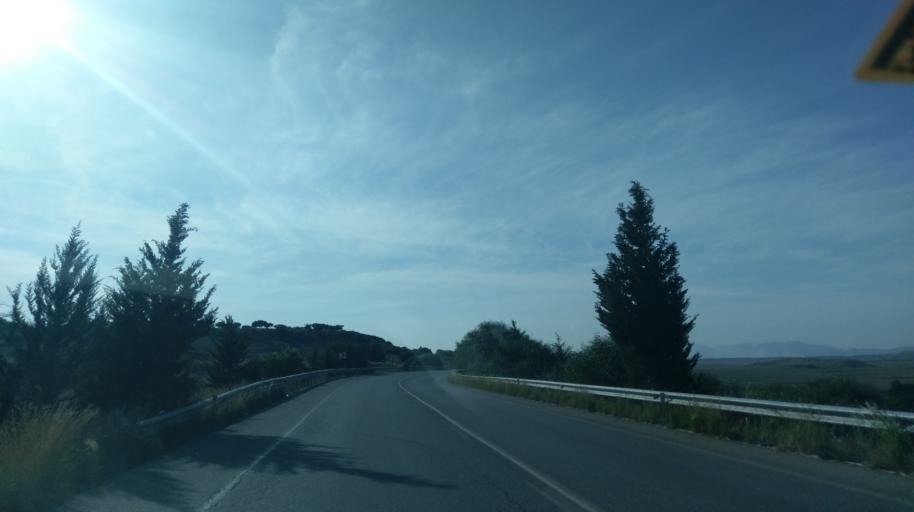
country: CY
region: Ammochostos
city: Trikomo
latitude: 35.2788
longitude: 33.8417
